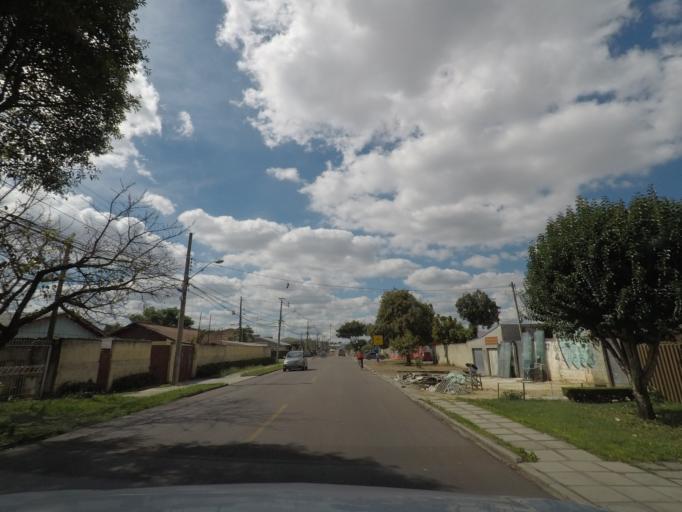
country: BR
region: Parana
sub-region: Sao Jose Dos Pinhais
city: Sao Jose dos Pinhais
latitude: -25.5058
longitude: -49.2219
